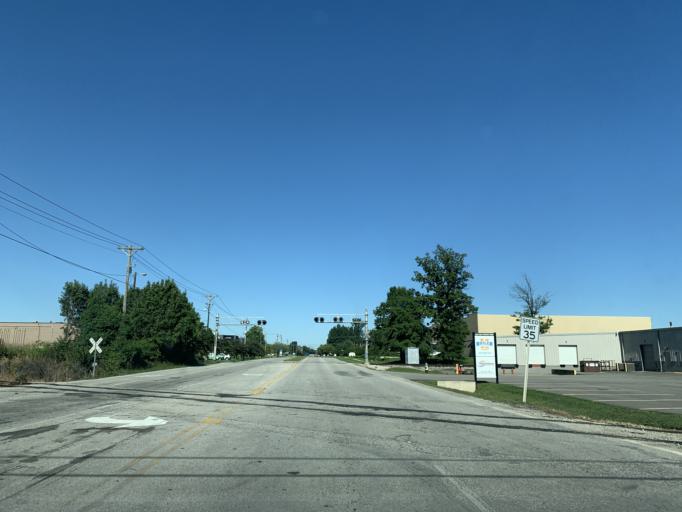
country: US
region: Kentucky
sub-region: Jefferson County
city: West Buechel
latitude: 38.1847
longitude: -85.6821
